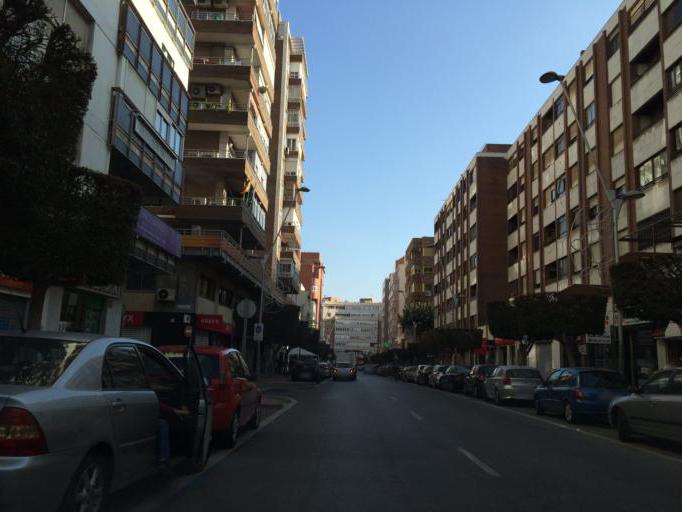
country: ES
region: Andalusia
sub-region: Provincia de Almeria
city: Almeria
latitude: 36.8375
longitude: -2.4586
